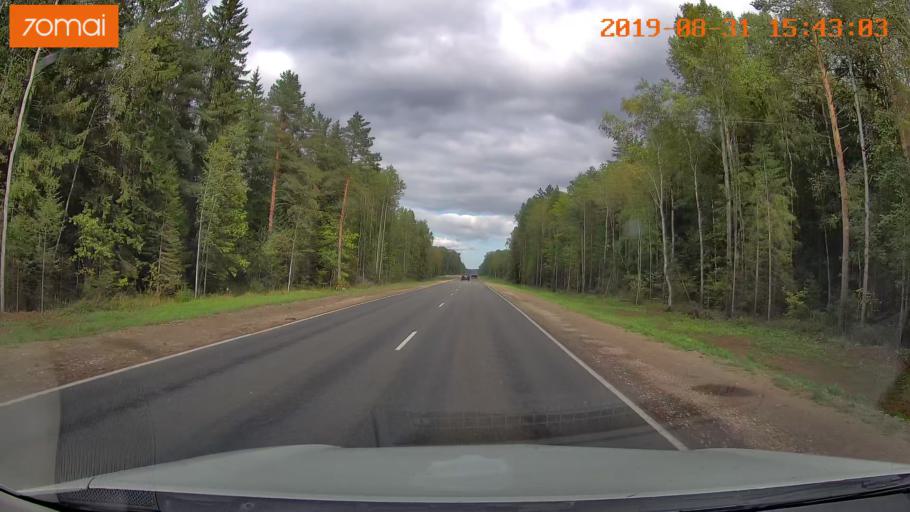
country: RU
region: Kaluga
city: Mosal'sk
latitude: 54.6504
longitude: 34.9015
